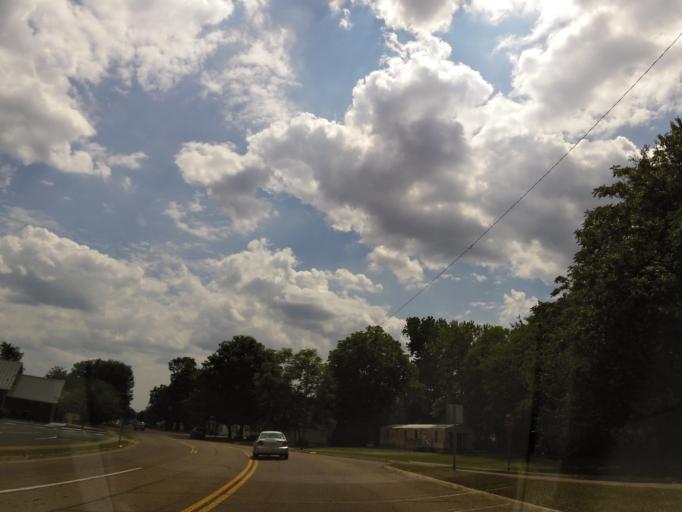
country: US
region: Tennessee
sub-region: Sequatchie County
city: Dunlap
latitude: 35.3768
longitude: -85.3880
